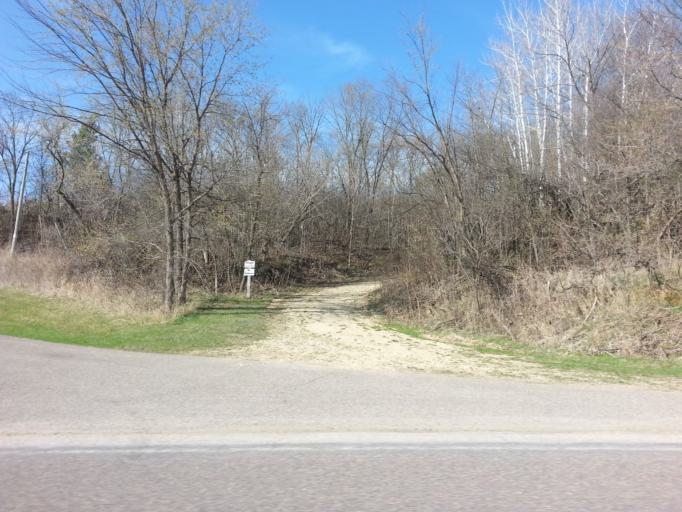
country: US
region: Wisconsin
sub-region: Pierce County
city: Ellsworth
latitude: 44.7202
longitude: -92.5760
